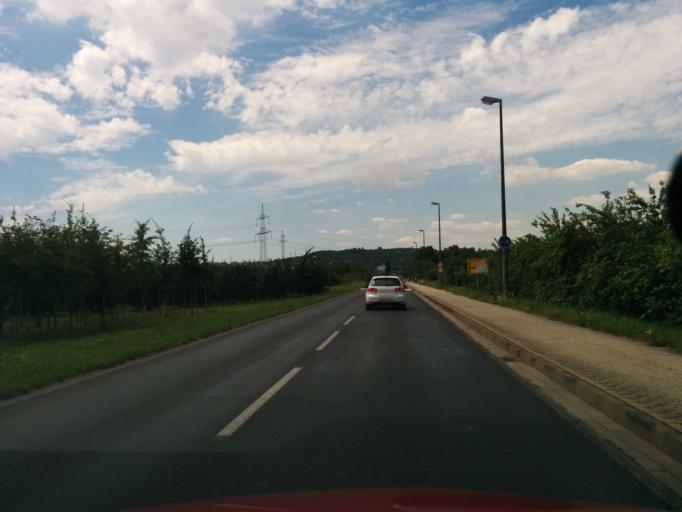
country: DE
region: Rheinland-Pfalz
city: Mulheim-Karlich
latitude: 50.3960
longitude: 7.5053
